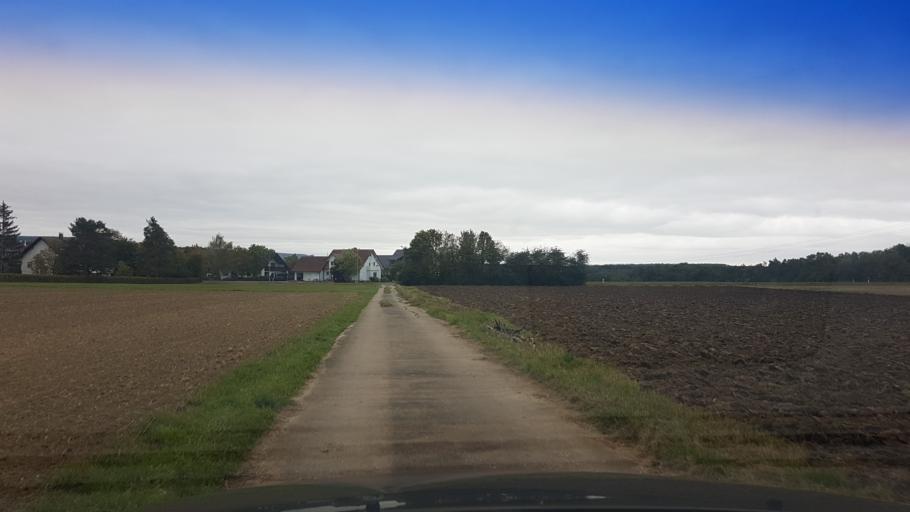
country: DE
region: Bavaria
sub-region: Upper Franconia
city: Memmelsdorf
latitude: 49.9347
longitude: 10.9763
